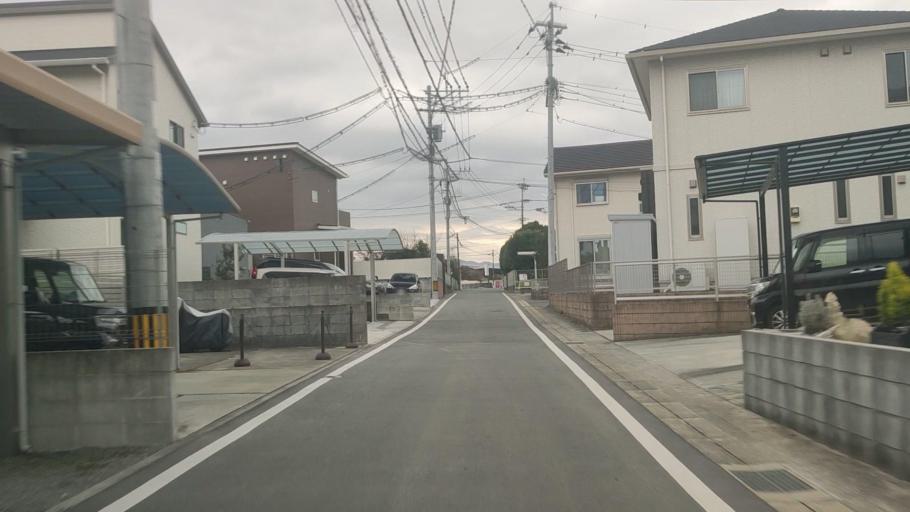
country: JP
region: Kumamoto
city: Ozu
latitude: 32.8284
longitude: 130.8006
